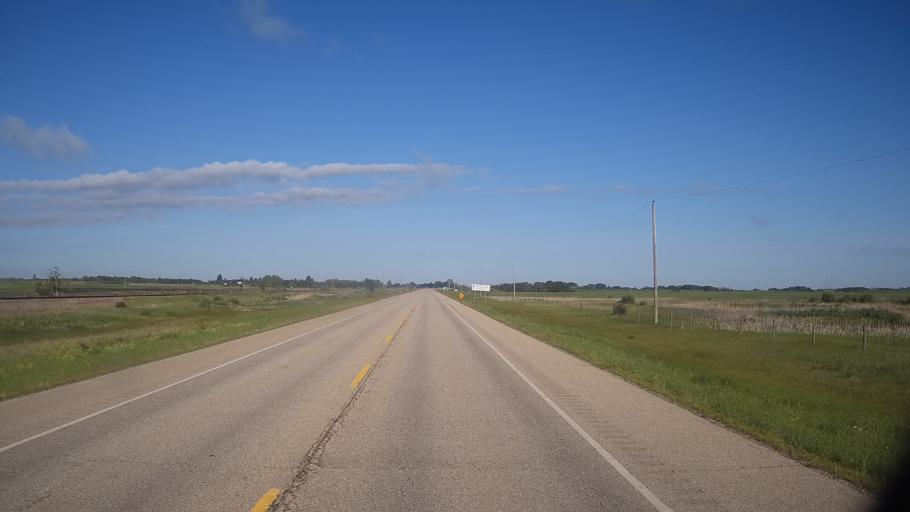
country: CA
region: Saskatchewan
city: Lanigan
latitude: 51.8690
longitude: -105.1606
